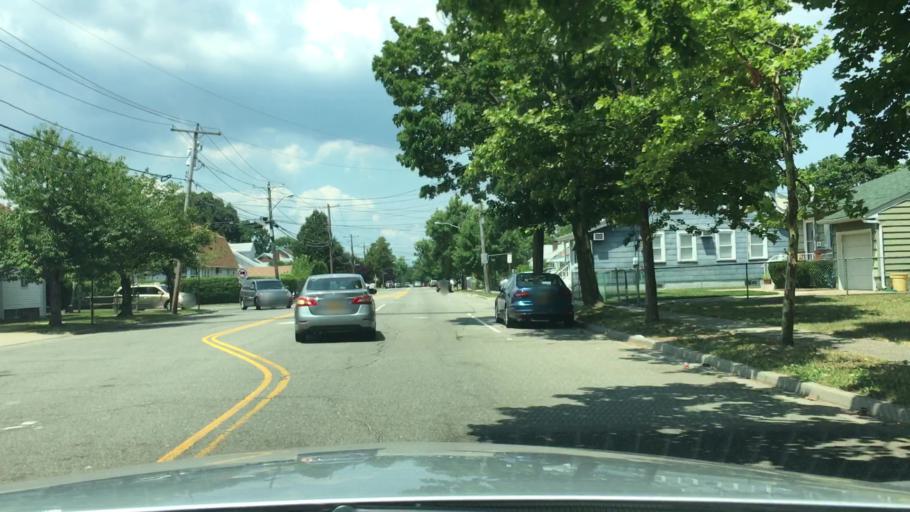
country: US
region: New York
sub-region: Nassau County
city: Hicksville
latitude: 40.7701
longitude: -73.5215
